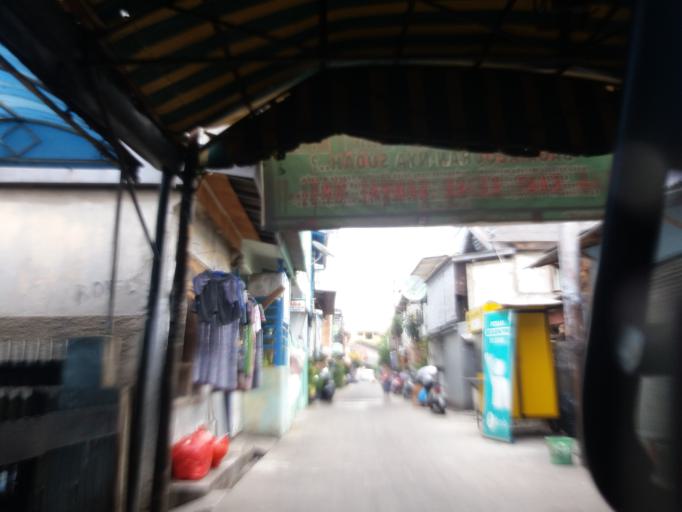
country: ID
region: Jakarta Raya
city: Jakarta
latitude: -6.2126
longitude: 106.8257
